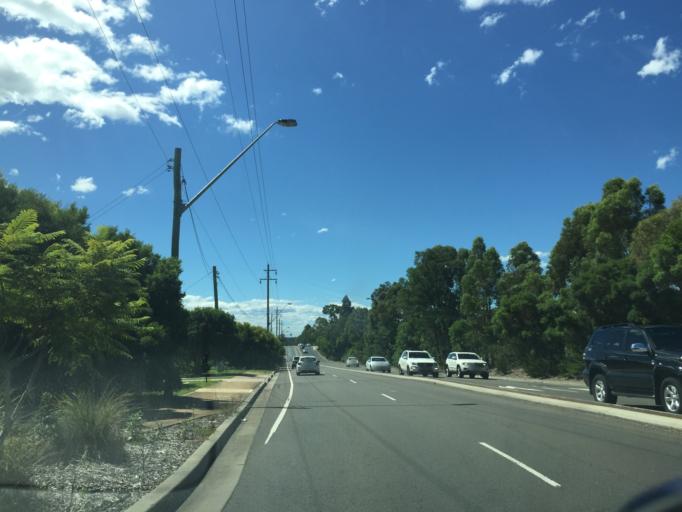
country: AU
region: New South Wales
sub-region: The Hills Shire
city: Glenhaven
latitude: -33.7090
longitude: 150.9738
